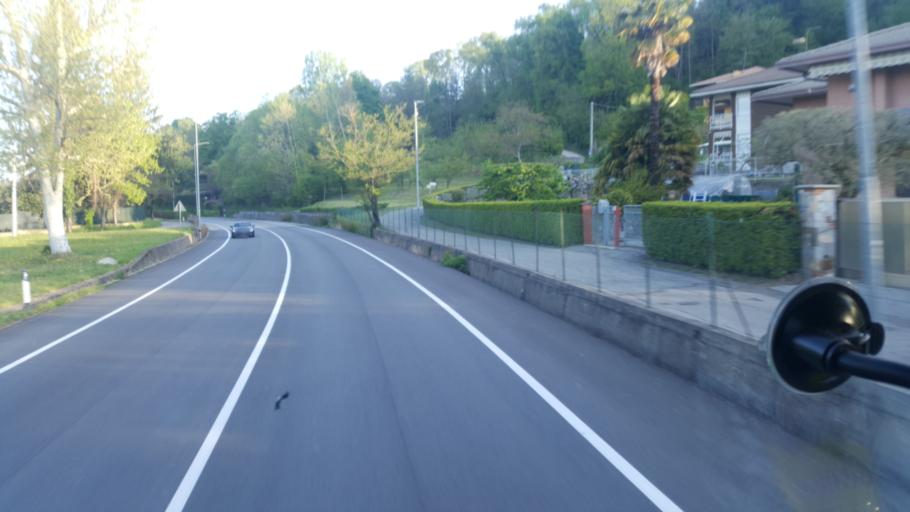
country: IT
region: Lombardy
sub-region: Provincia di Varese
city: Barasso
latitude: 45.8168
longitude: 8.7601
